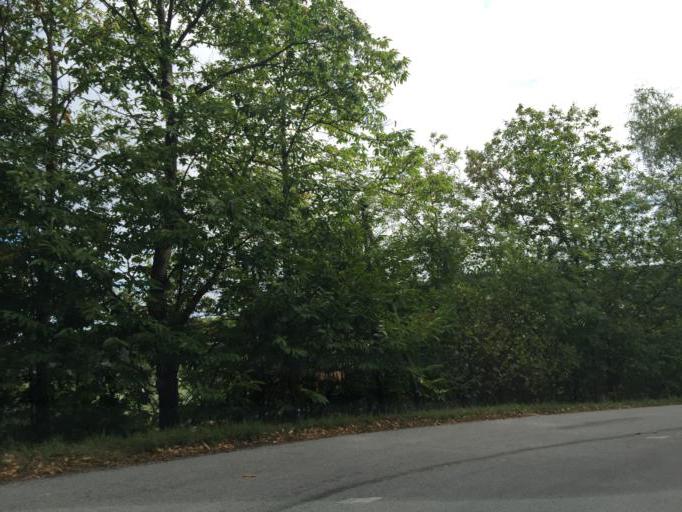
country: FR
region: Rhone-Alpes
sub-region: Departement de la Loire
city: Pelussin
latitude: 45.4653
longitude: 4.6652
